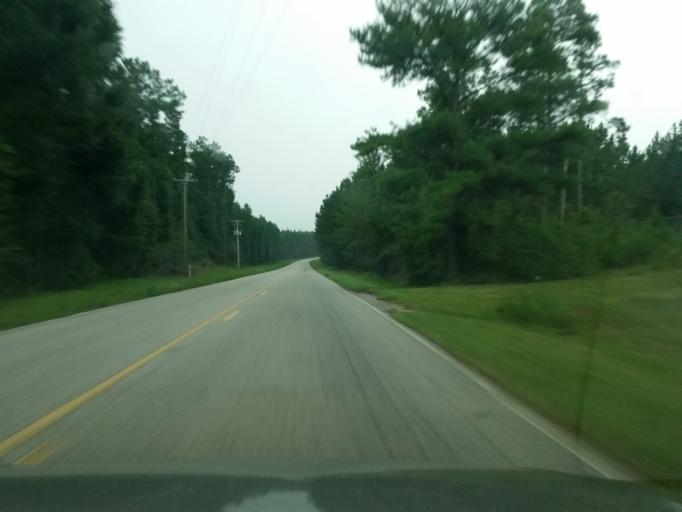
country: US
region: Florida
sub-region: Escambia County
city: Cantonment
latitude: 30.6936
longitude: -87.5112
